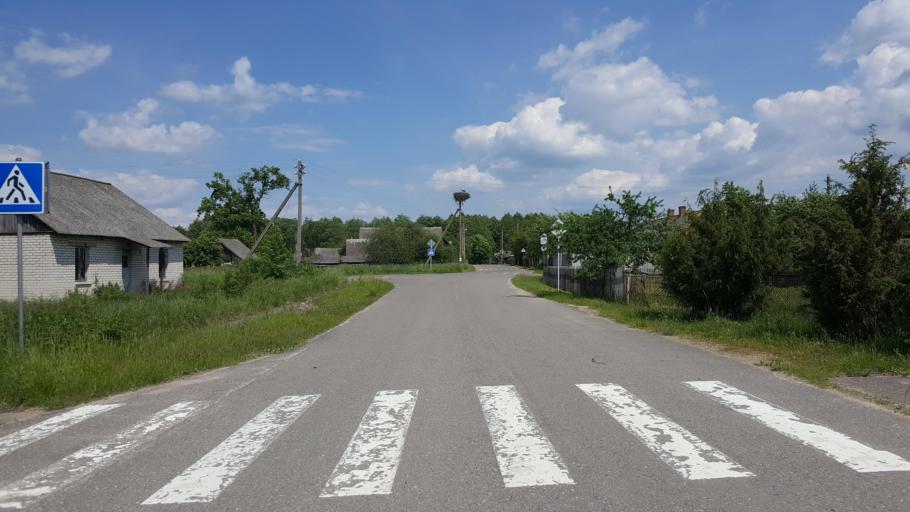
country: BY
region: Brest
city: Zhabinka
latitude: 52.4760
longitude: 24.1502
